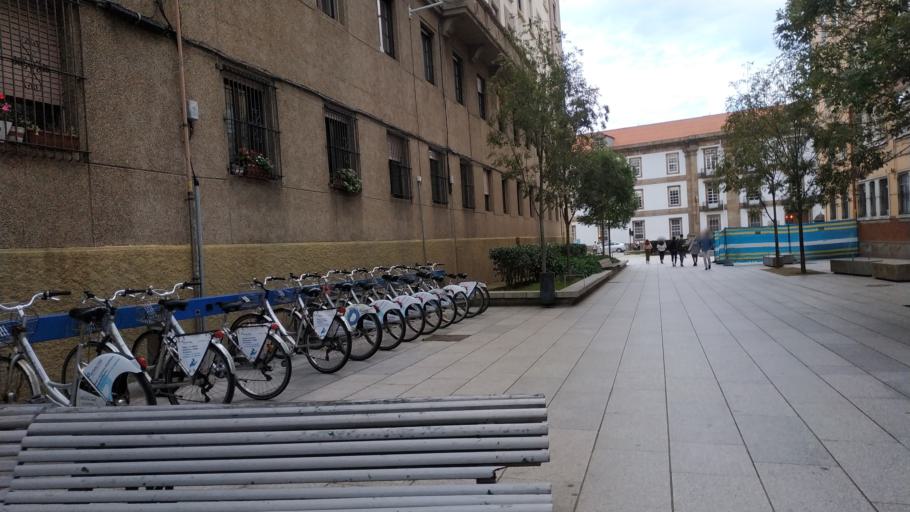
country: ES
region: Galicia
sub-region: Provincia da Coruna
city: A Coruna
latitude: 43.3728
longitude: -8.3965
